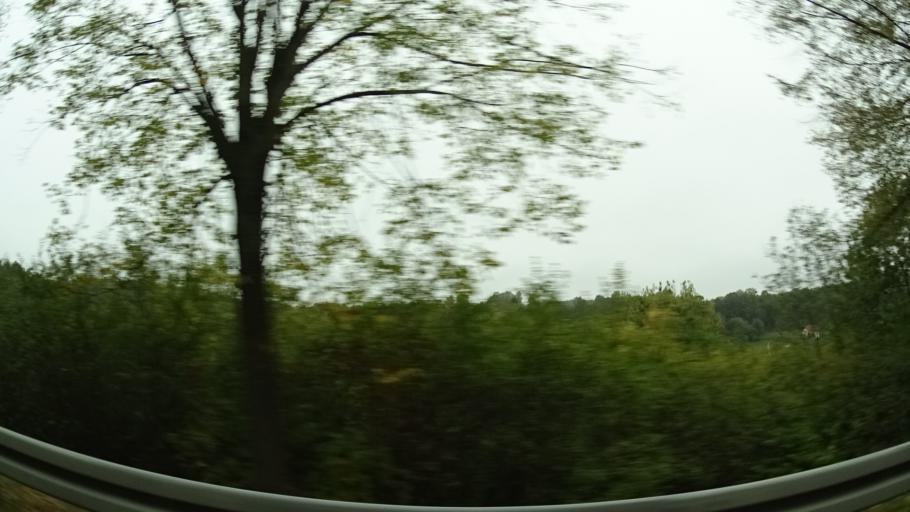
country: DE
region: Hesse
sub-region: Regierungsbezirk Kassel
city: Hilders
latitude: 50.5663
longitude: 10.0049
